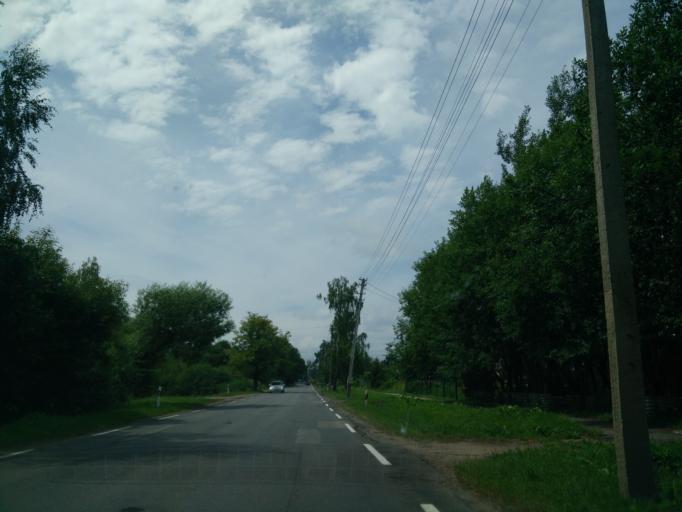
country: LT
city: Skaidiskes
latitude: 54.6932
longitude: 25.4549
